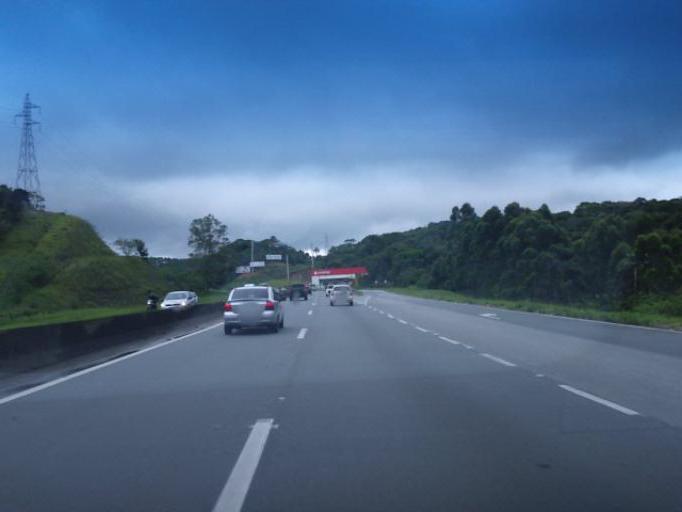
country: BR
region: Santa Catarina
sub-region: Balneario Camboriu
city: Balneario Camboriu
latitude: -26.9618
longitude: -48.6819
